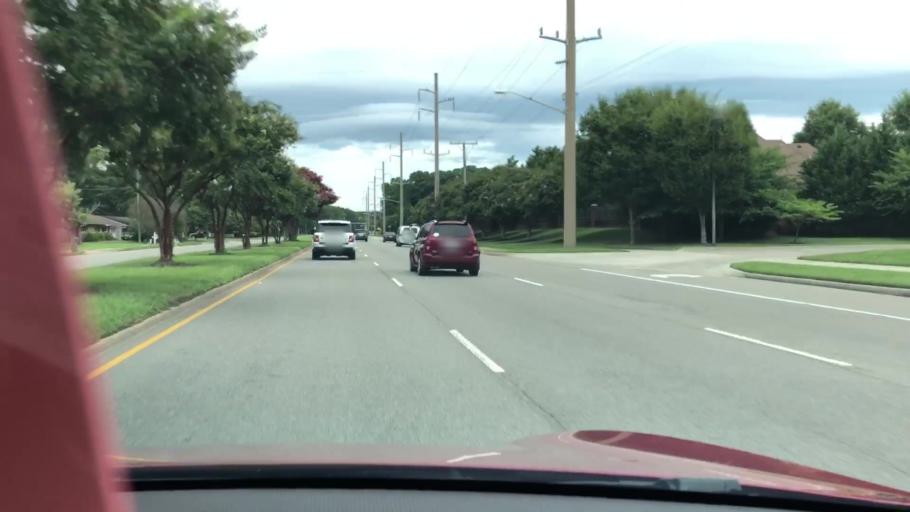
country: US
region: Virginia
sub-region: City of Virginia Beach
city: Virginia Beach
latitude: 36.8821
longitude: -76.0452
